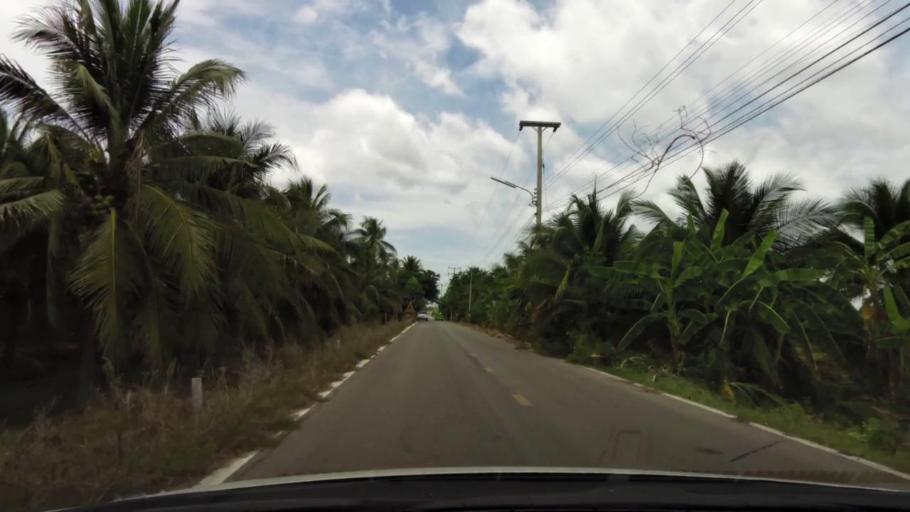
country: TH
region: Ratchaburi
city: Damnoen Saduak
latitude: 13.5224
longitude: 100.0104
